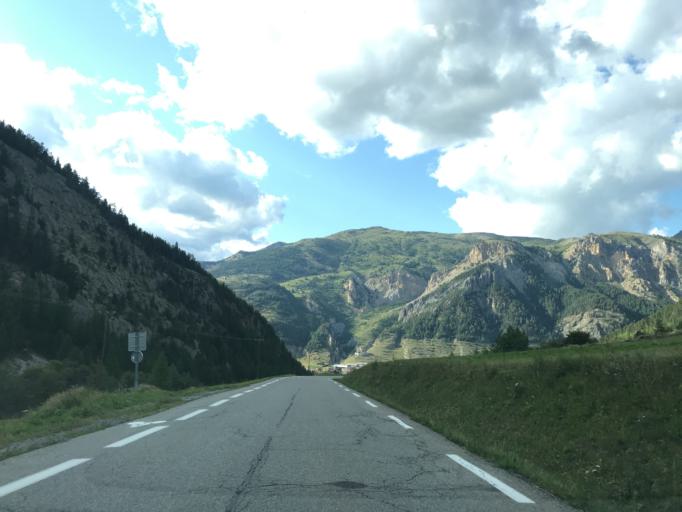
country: IT
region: Piedmont
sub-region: Provincia di Torino
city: Claviere
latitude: 44.8580
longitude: 6.7255
